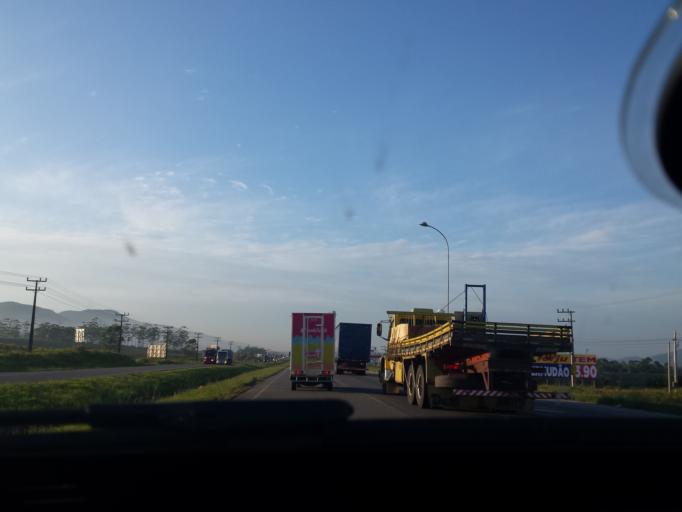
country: BR
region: Santa Catarina
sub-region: Imbituba
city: Imbituba
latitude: -28.1942
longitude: -48.6973
